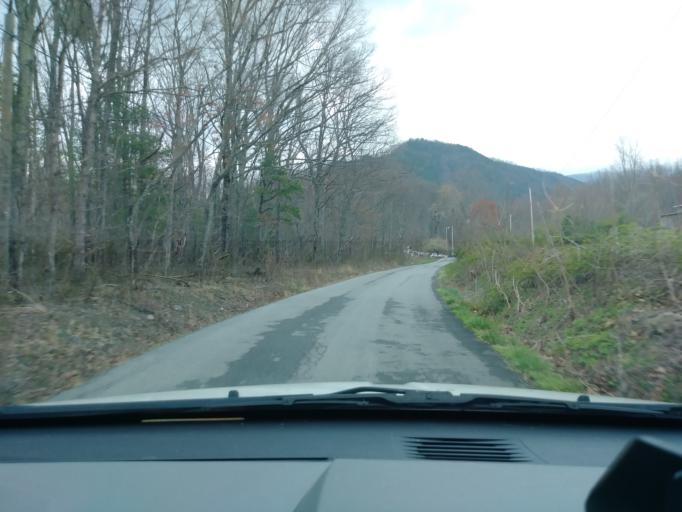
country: US
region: Tennessee
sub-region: Greene County
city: Tusculum
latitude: 36.0722
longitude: -82.7215
